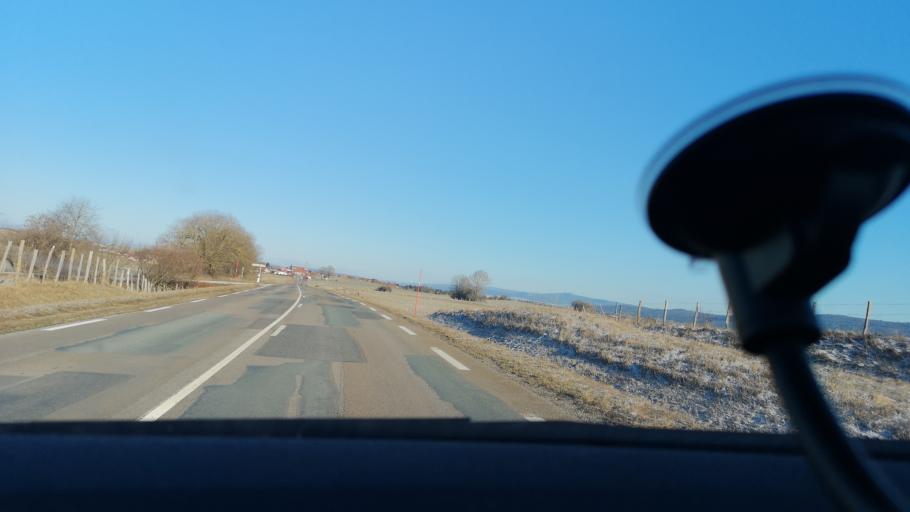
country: FR
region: Franche-Comte
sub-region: Departement du Doubs
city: Frasne
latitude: 46.8439
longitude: 6.1379
